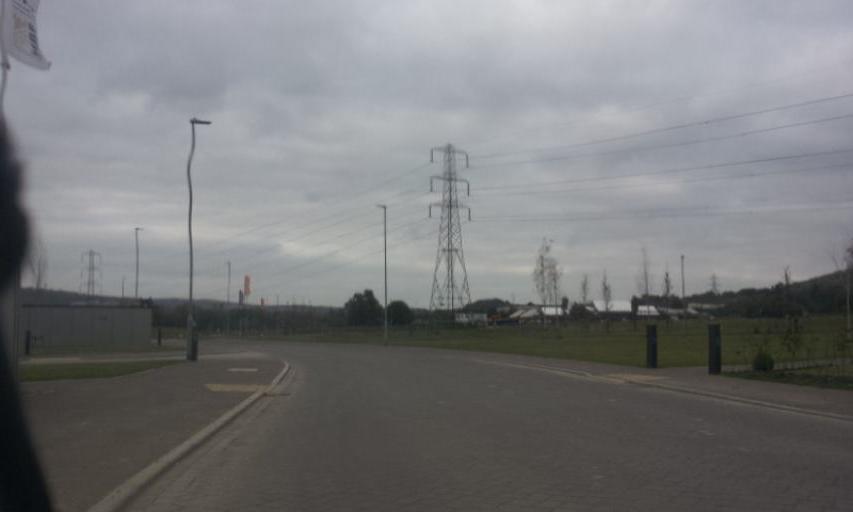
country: GB
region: England
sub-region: Medway
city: Halling
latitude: 51.3405
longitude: 0.4579
